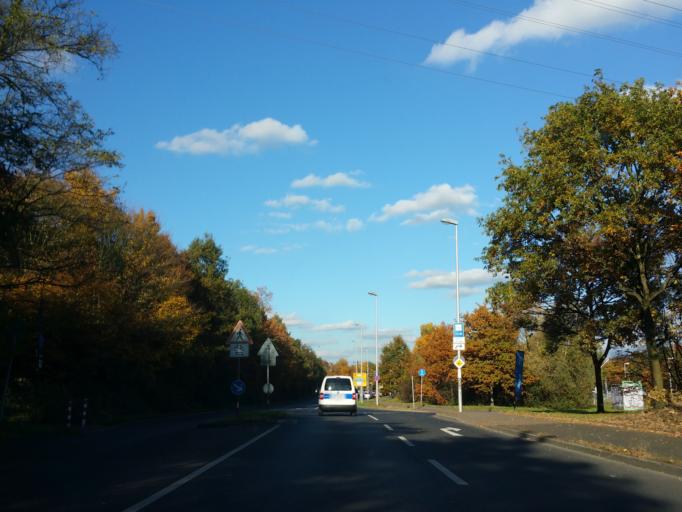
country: DE
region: North Rhine-Westphalia
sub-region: Regierungsbezirk Dusseldorf
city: Dusseldorf
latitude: 51.1937
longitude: 6.7995
